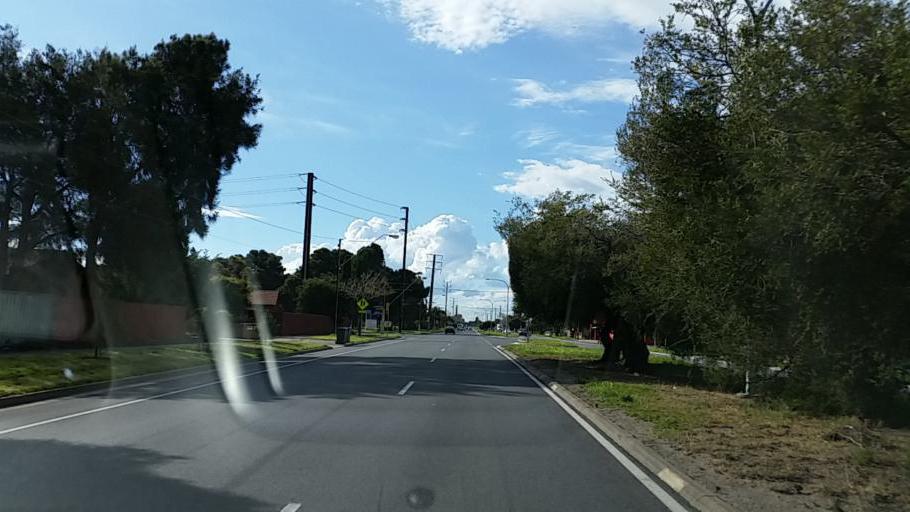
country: AU
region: South Australia
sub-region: Port Adelaide Enfield
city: Birkenhead
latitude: -34.7973
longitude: 138.5014
